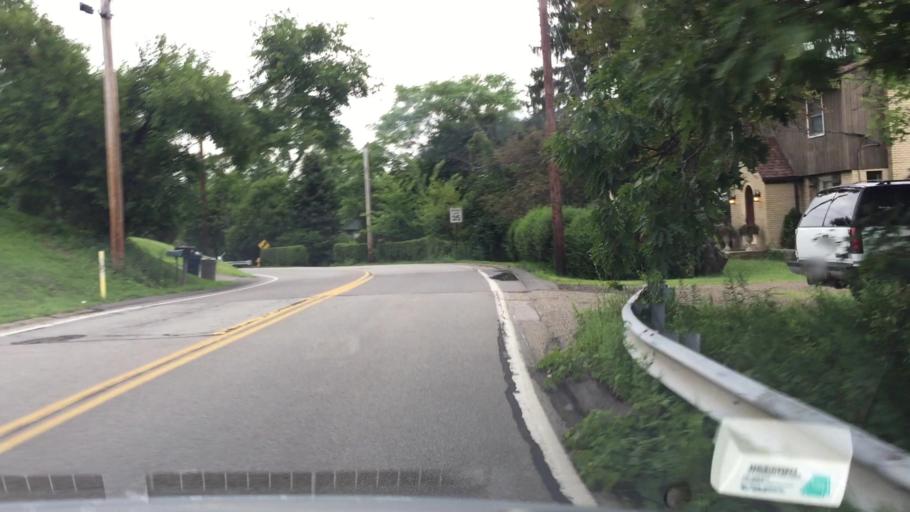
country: US
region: Pennsylvania
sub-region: Allegheny County
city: Glenshaw
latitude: 40.5161
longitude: -79.9802
